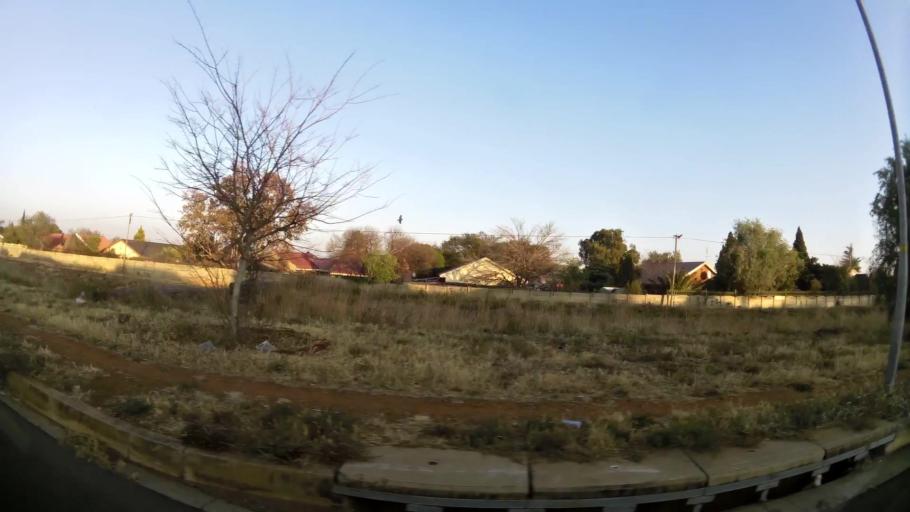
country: ZA
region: Orange Free State
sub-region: Mangaung Metropolitan Municipality
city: Bloemfontein
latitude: -29.0999
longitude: 26.1635
